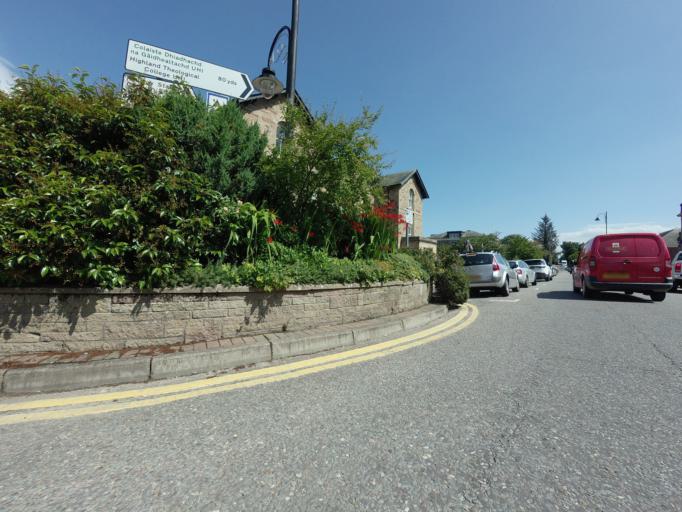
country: GB
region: Scotland
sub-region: Highland
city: Dingwall
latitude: 57.5952
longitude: -4.4251
